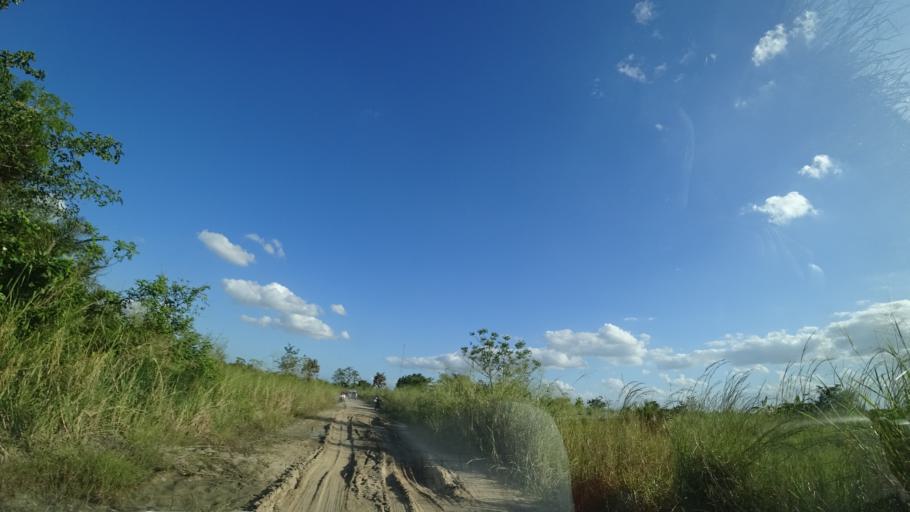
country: MZ
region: Sofala
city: Dondo
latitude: -19.3744
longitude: 34.5922
